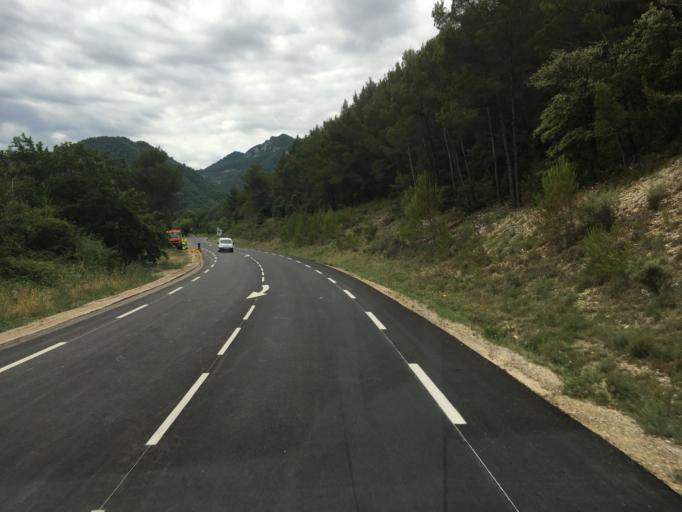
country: FR
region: Rhone-Alpes
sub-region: Departement de la Drome
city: Nyons
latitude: 44.3829
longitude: 5.1714
